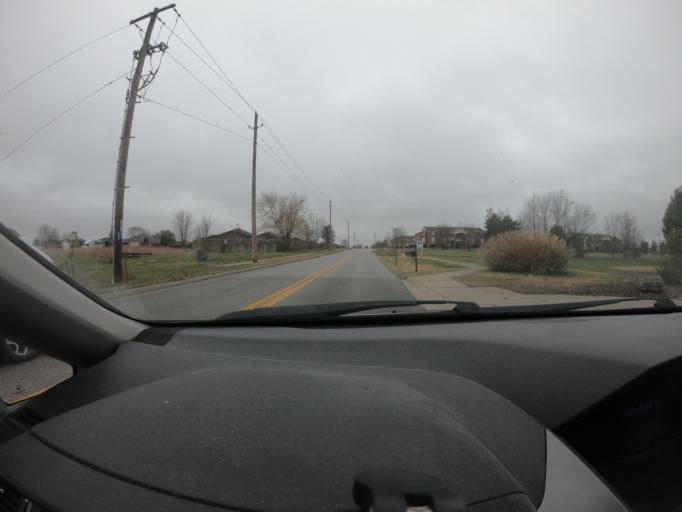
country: US
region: Arkansas
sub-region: Benton County
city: Bentonville
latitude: 36.3569
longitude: -94.2401
